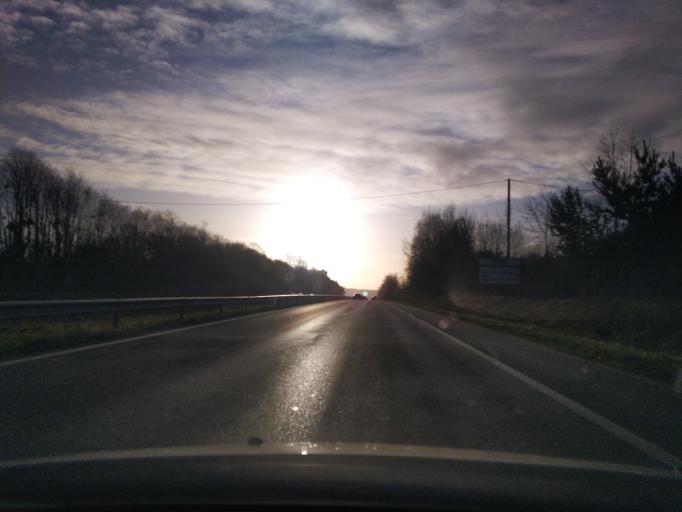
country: FR
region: Haute-Normandie
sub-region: Departement de la Seine-Maritime
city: Maromme
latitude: 49.4762
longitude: 1.0205
